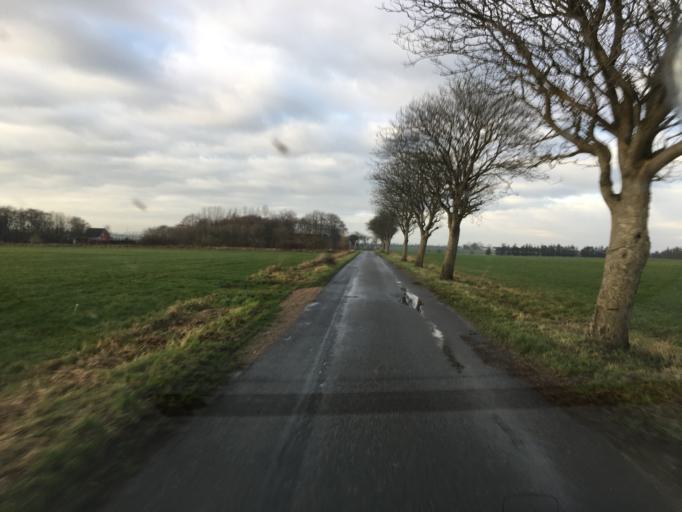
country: DK
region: South Denmark
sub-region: Tonder Kommune
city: Logumkloster
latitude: 55.1150
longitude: 8.8729
